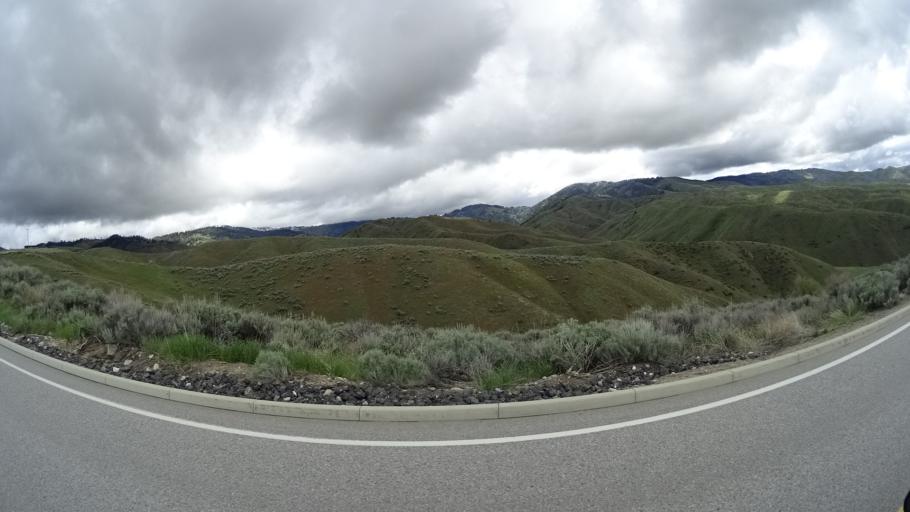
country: US
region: Idaho
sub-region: Ada County
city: Boise
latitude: 43.7057
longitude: -116.1658
